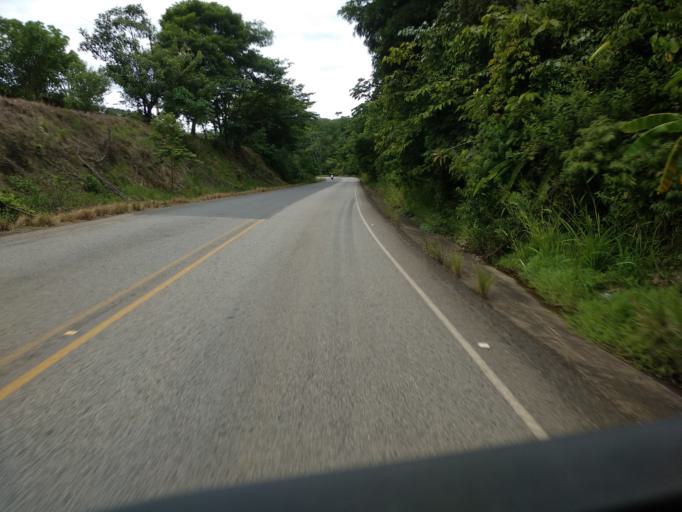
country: CR
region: Puntarenas
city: Buenos Aires
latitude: 9.0983
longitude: -83.2801
